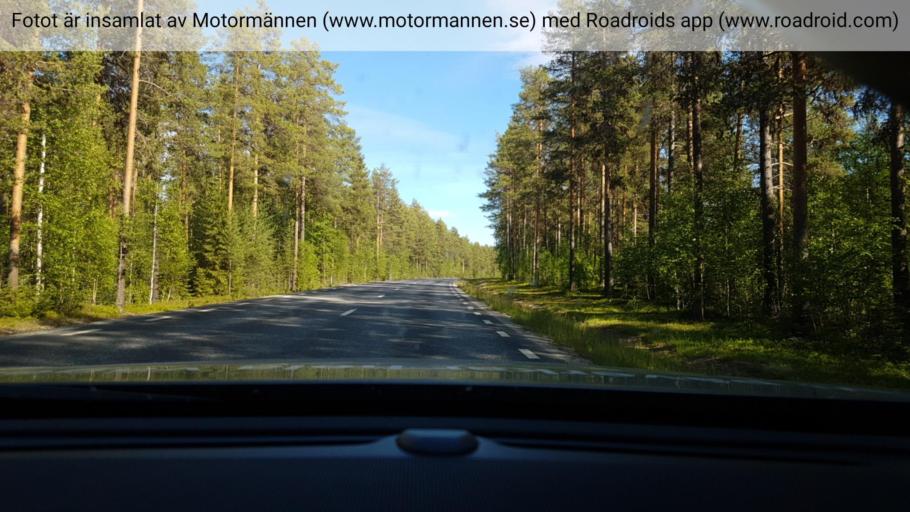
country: SE
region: Vaesterbotten
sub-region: Lycksele Kommun
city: Soderfors
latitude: 64.7084
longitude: 18.3091
